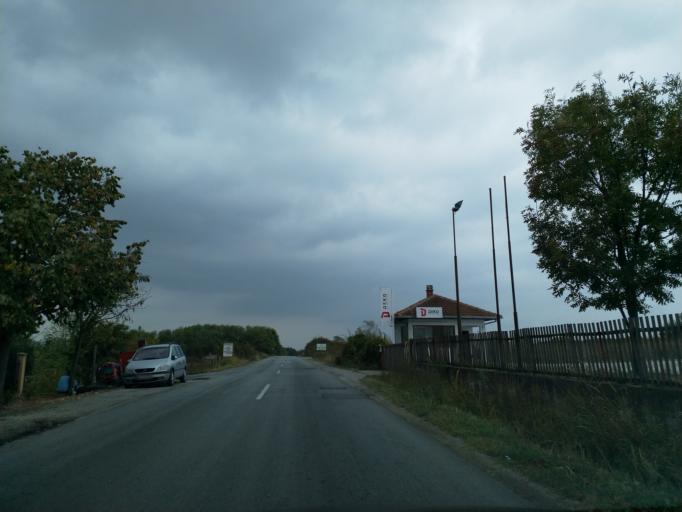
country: RS
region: Central Serbia
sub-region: Pomoravski Okrug
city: Jagodina
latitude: 44.0177
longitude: 21.1980
